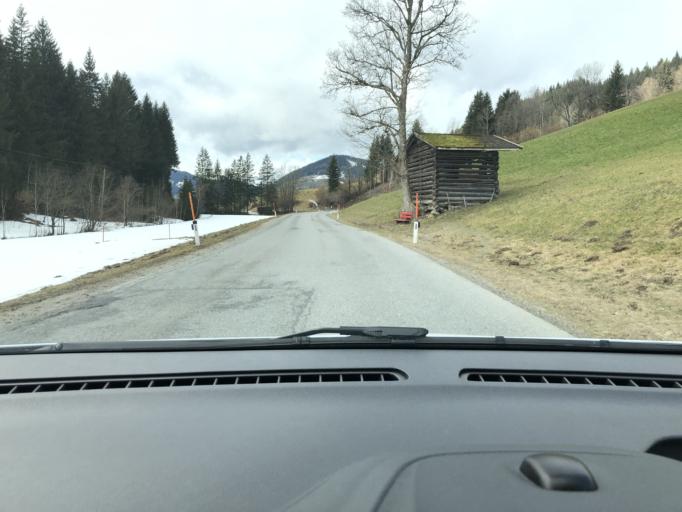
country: AT
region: Tyrol
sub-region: Politischer Bezirk Kitzbuhel
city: Itter
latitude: 47.4503
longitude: 12.1150
